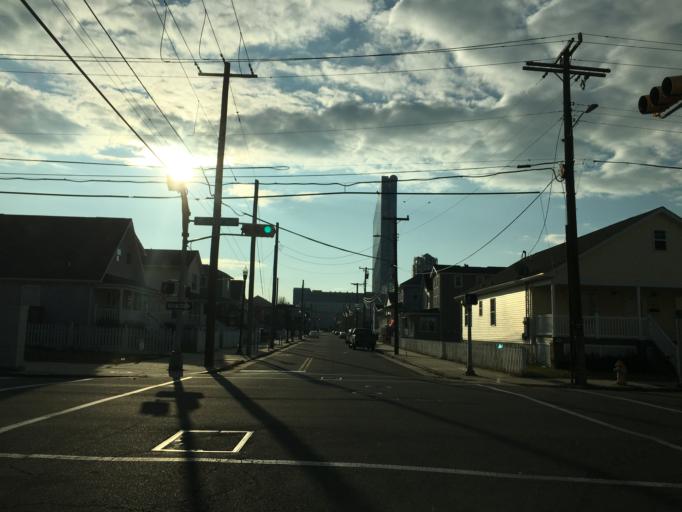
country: US
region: New Jersey
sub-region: Atlantic County
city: Atlantic City
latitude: 39.3696
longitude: -74.4188
